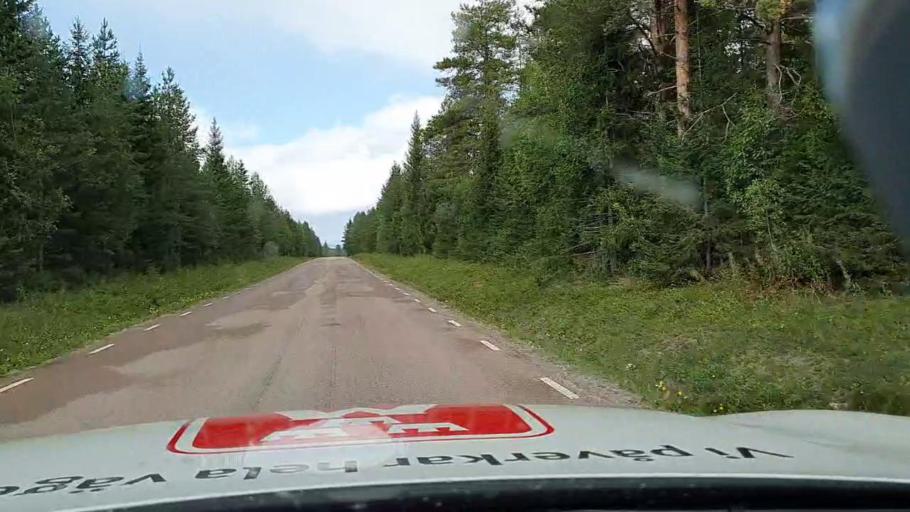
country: SE
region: Jaemtland
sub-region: Stroemsunds Kommun
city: Stroemsund
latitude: 63.8728
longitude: 15.3658
